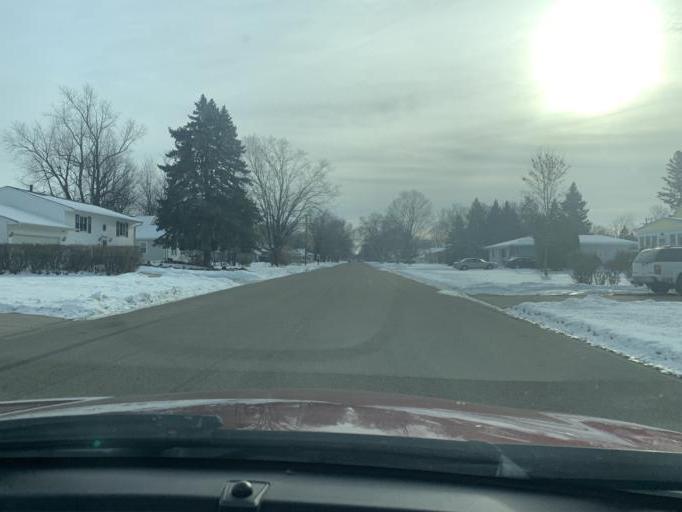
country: US
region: Minnesota
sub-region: Washington County
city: Saint Paul Park
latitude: 44.8394
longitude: -92.9856
